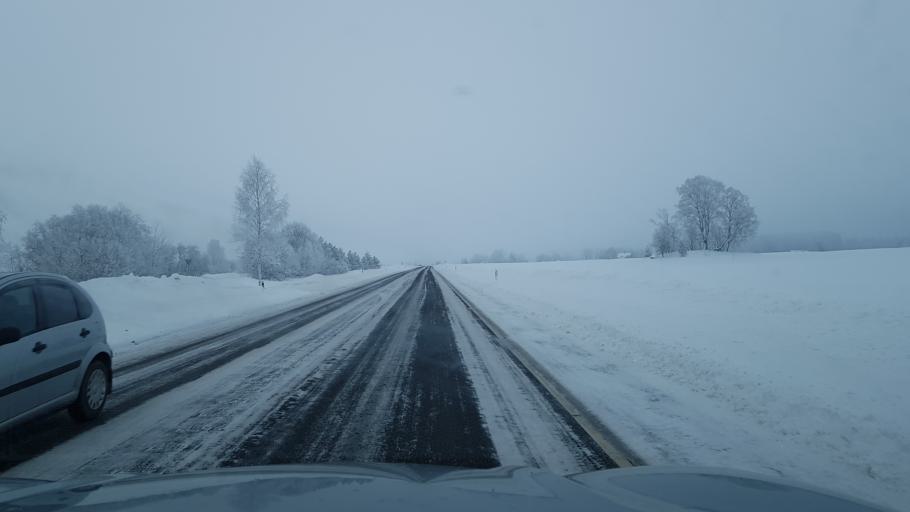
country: EE
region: Ida-Virumaa
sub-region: Johvi vald
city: Johvi
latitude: 59.2464
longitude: 27.3684
